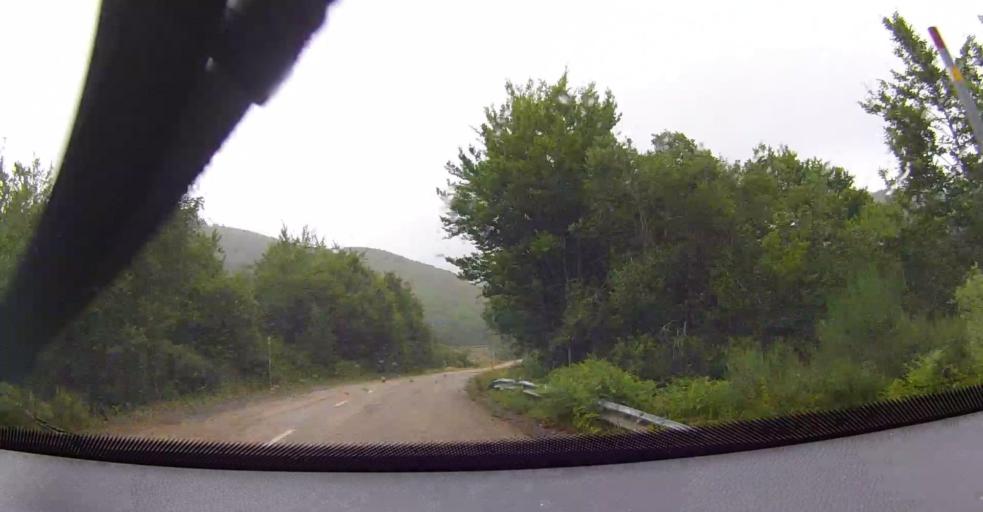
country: ES
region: Castille and Leon
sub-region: Provincia de Leon
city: Puebla de Lillo
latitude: 43.0647
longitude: -5.2698
